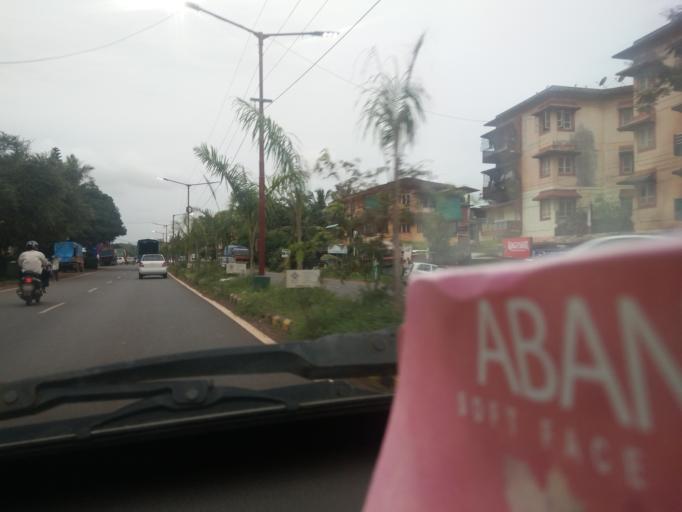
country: IN
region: Goa
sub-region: South Goa
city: Raia
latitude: 15.2925
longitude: 73.9756
